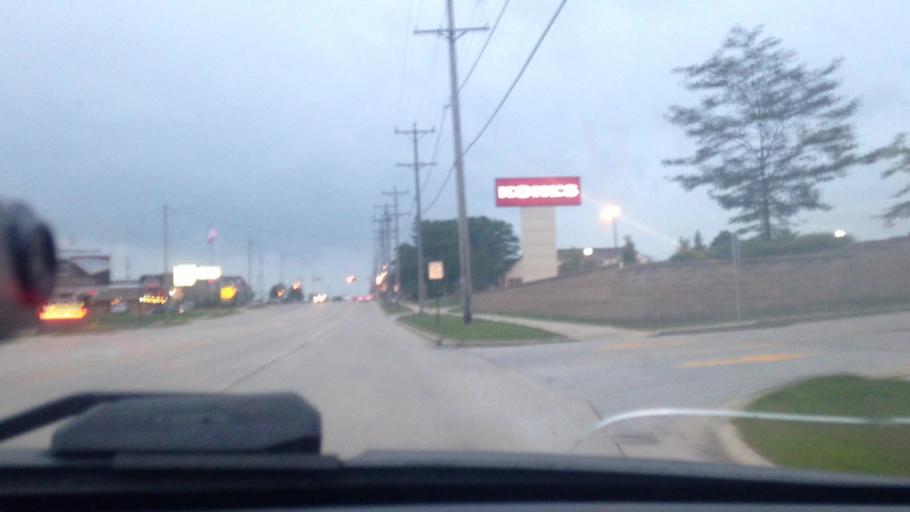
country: US
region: Wisconsin
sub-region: Washington County
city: West Bend
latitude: 43.4036
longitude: -88.1813
